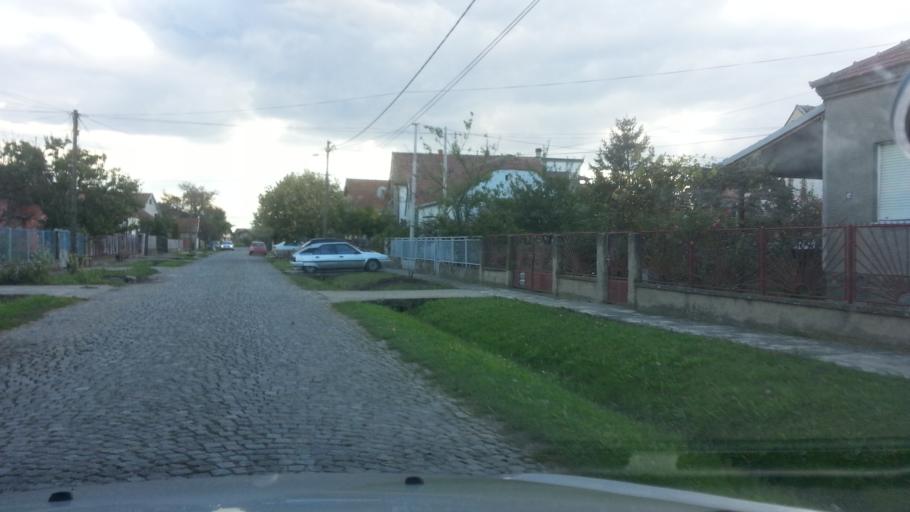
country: RS
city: Novi Banovci
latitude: 44.9081
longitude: 20.2615
